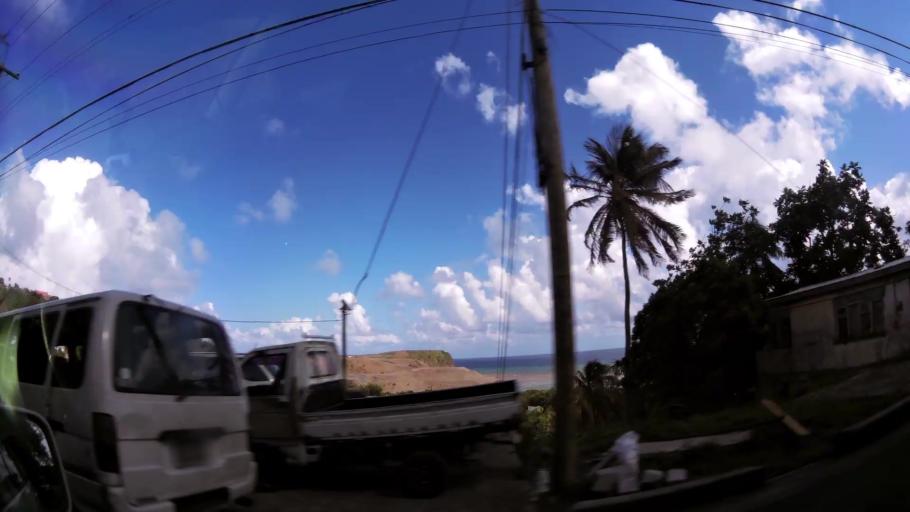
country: VC
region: Charlotte
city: Biabou
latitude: 13.1469
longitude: -61.1598
